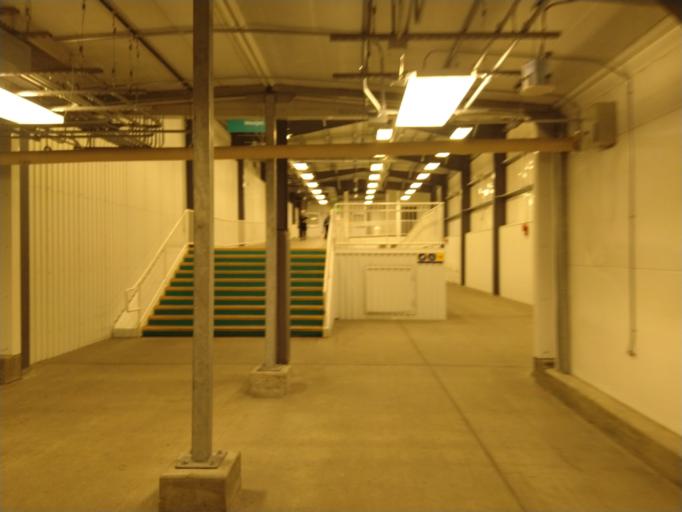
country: CA
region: Alberta
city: Calgary
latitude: 51.1338
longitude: -114.0124
